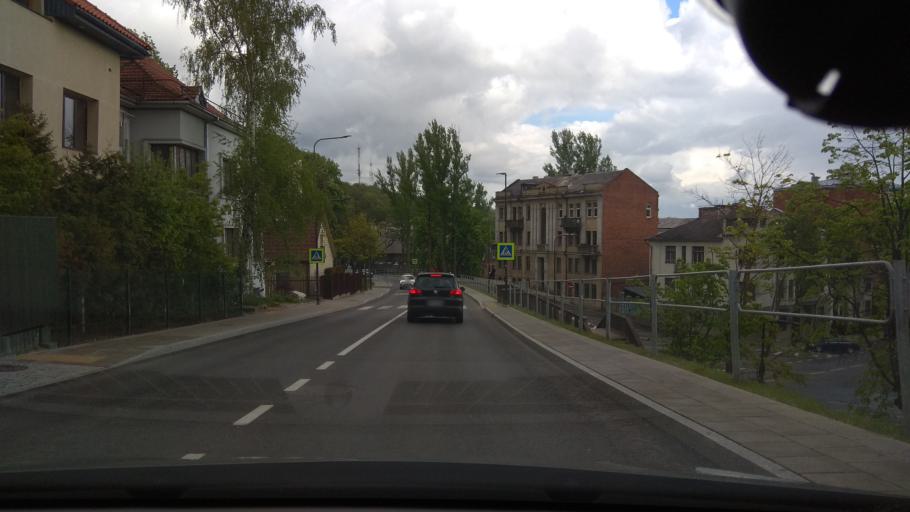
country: LT
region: Kauno apskritis
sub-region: Kaunas
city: Kaunas
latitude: 54.9003
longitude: 23.9214
